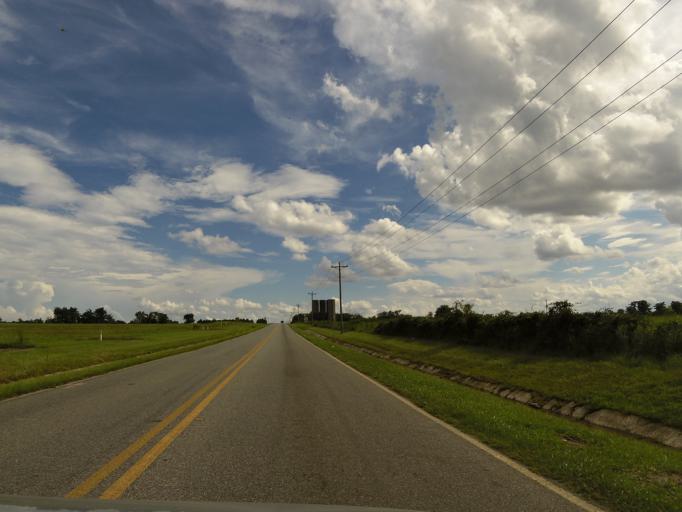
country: US
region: Florida
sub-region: Clay County
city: Green Cove Springs
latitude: 30.0201
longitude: -81.7314
